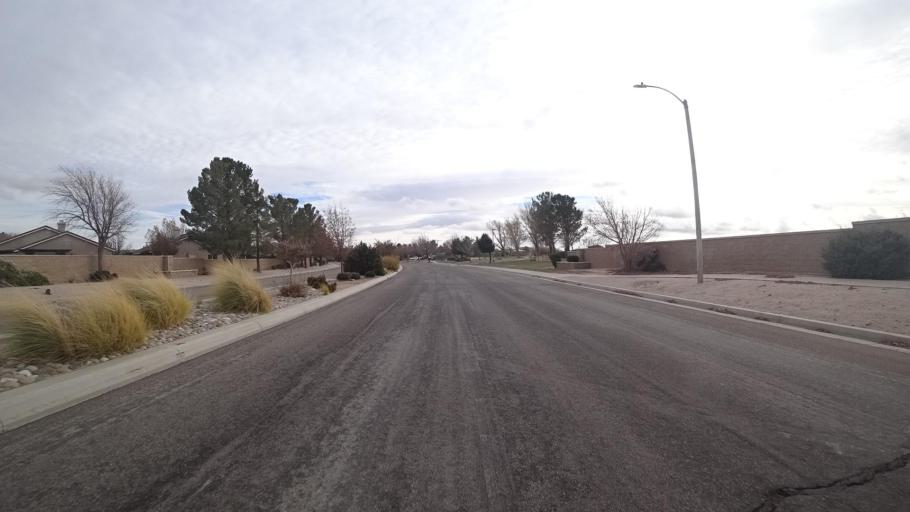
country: US
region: California
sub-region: Kern County
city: Rosamond
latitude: 34.8544
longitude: -118.2025
